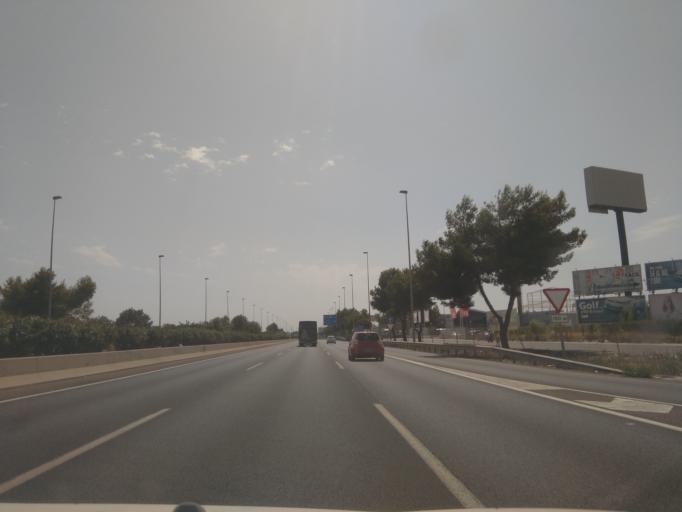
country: ES
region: Valencia
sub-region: Provincia de Valencia
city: Catarroja
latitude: 39.3947
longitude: -0.3910
